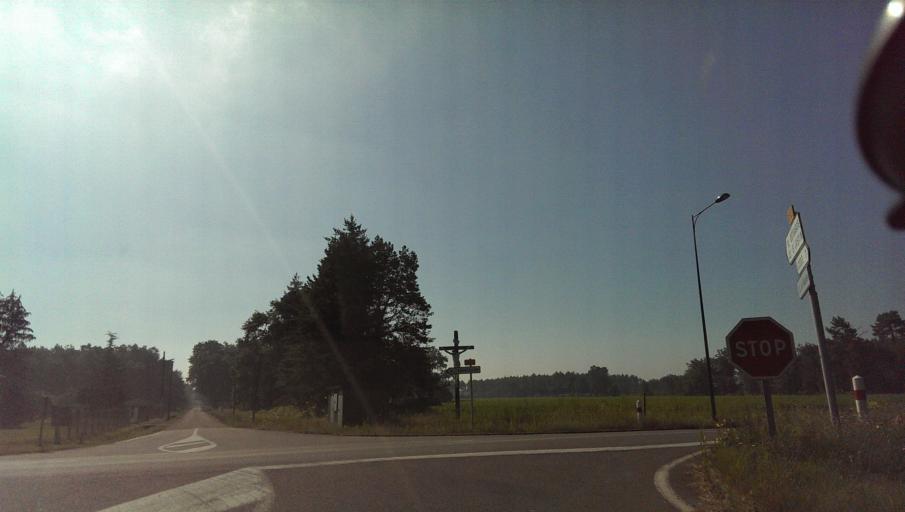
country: FR
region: Aquitaine
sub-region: Departement des Landes
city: Gabarret
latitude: 44.1029
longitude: -0.0148
